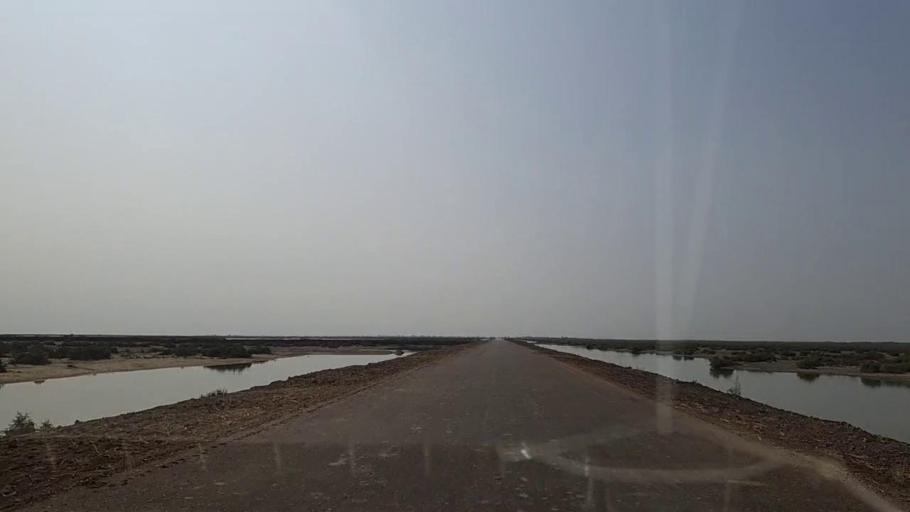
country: PK
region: Sindh
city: Chuhar Jamali
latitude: 24.2226
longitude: 67.8786
